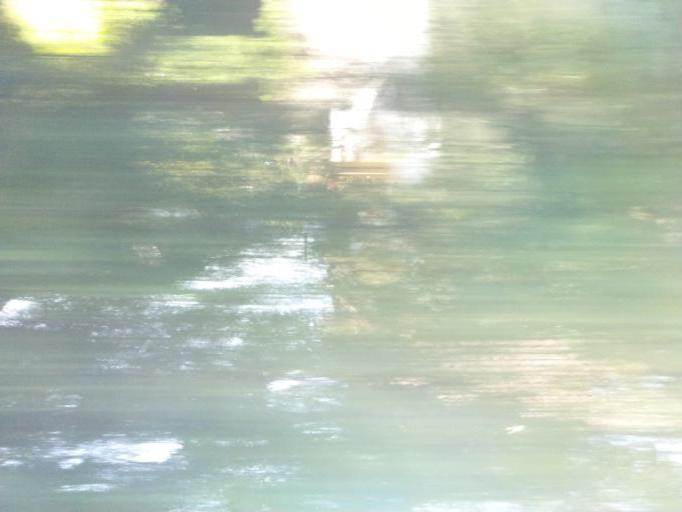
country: DE
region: Baden-Wuerttemberg
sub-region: Freiburg Region
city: Dogern
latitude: 47.6112
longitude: 8.1720
